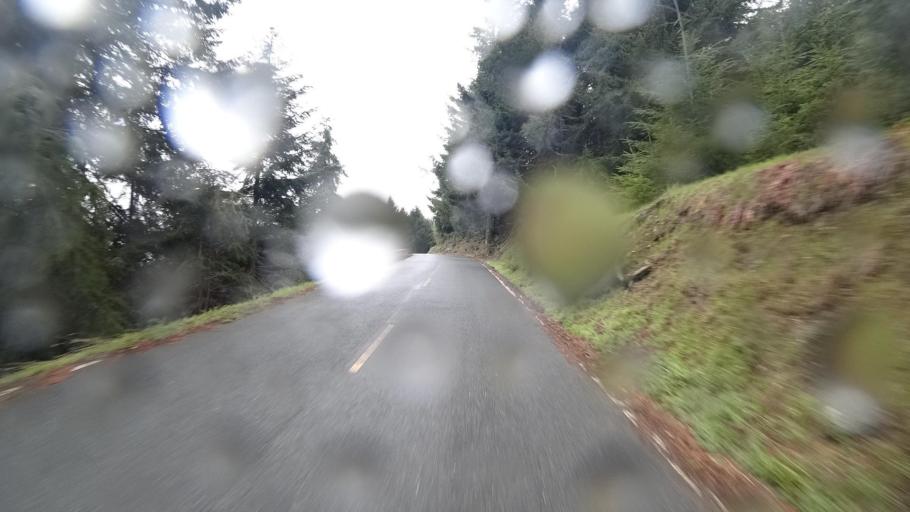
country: US
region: California
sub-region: Humboldt County
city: Willow Creek
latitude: 41.1503
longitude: -123.8251
